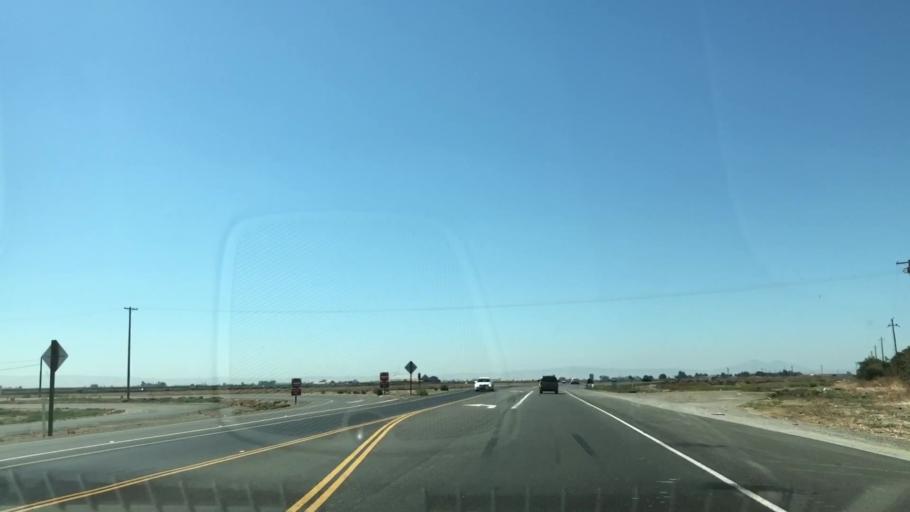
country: US
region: California
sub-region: San Joaquin County
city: Country Club
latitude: 37.9278
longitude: -121.3313
